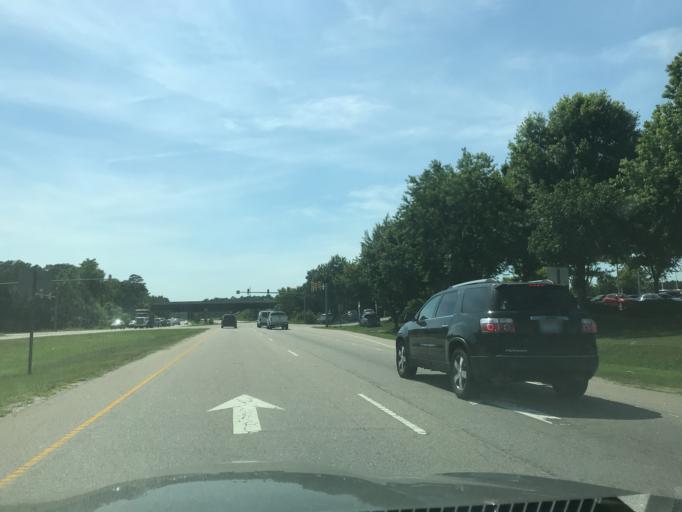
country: US
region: North Carolina
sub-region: Wake County
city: Wendell
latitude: 35.8037
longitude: -78.4231
